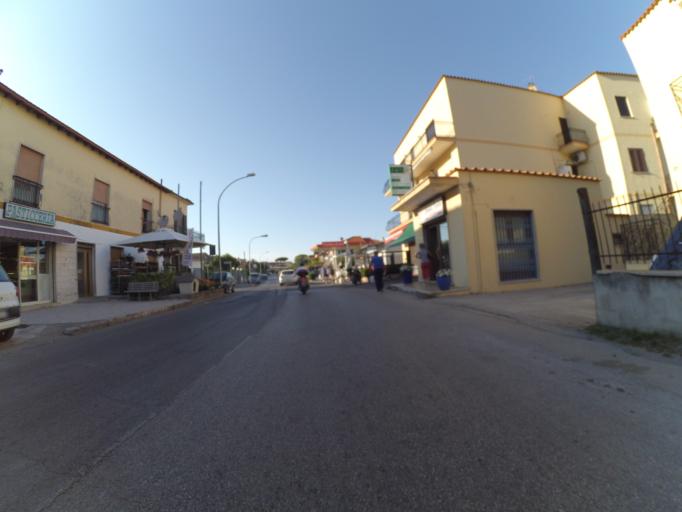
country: IT
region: Latium
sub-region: Provincia di Latina
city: San Felice Circeo
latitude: 41.2438
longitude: 13.0928
